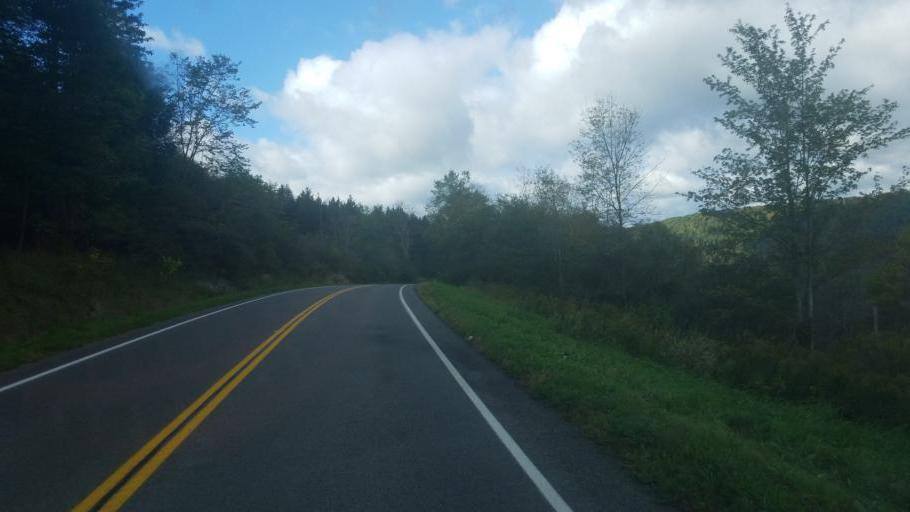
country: US
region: New York
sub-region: Allegany County
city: Cuba
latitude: 42.1447
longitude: -78.3111
